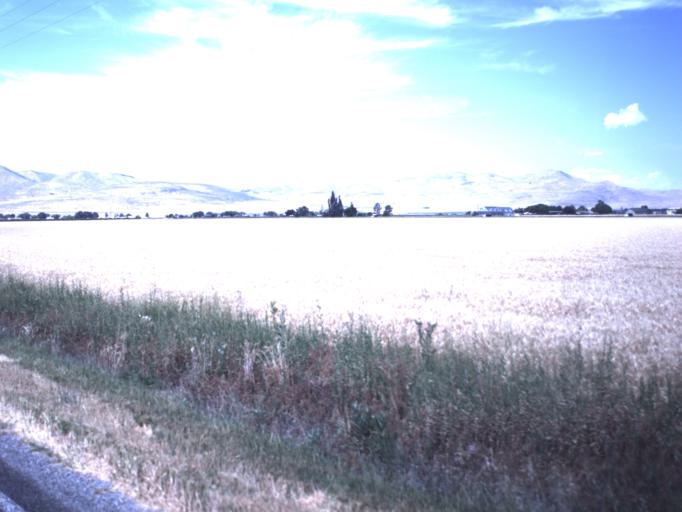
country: US
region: Utah
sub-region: Box Elder County
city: Tremonton
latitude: 41.7102
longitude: -112.2325
